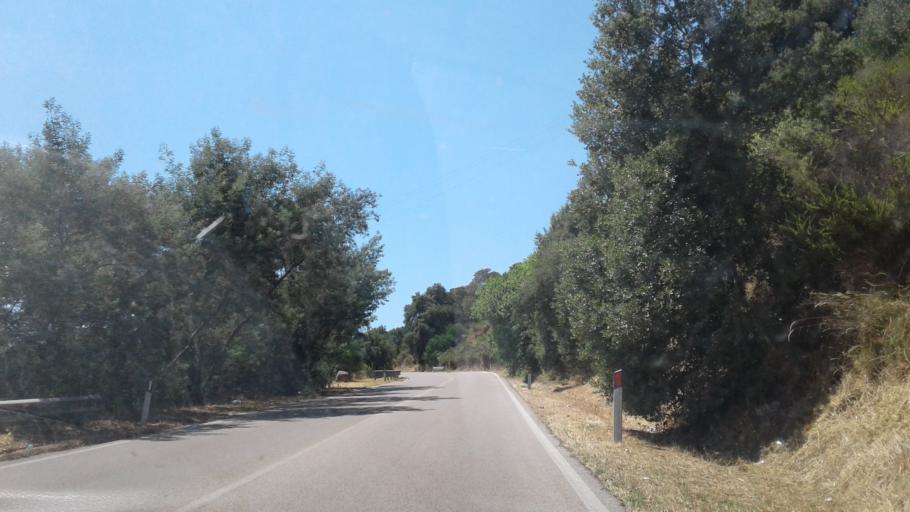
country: IT
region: Sardinia
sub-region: Provincia di Olbia-Tempio
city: Luras
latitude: 40.9305
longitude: 9.1815
